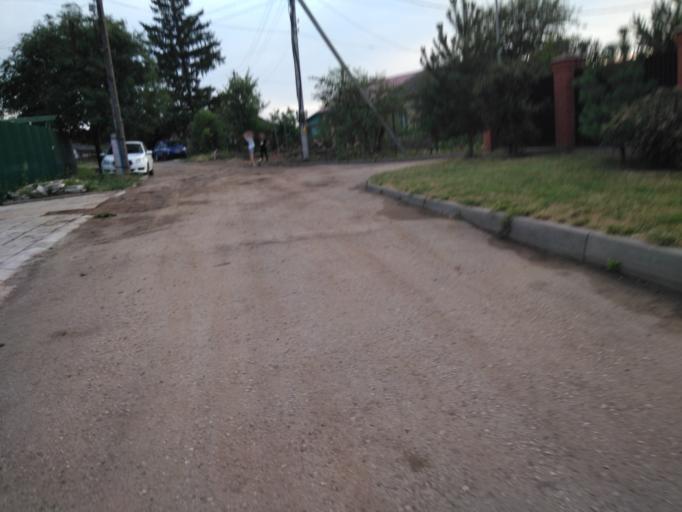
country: RU
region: Tula
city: Lomintsevskiy
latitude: 53.9365
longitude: 37.6213
